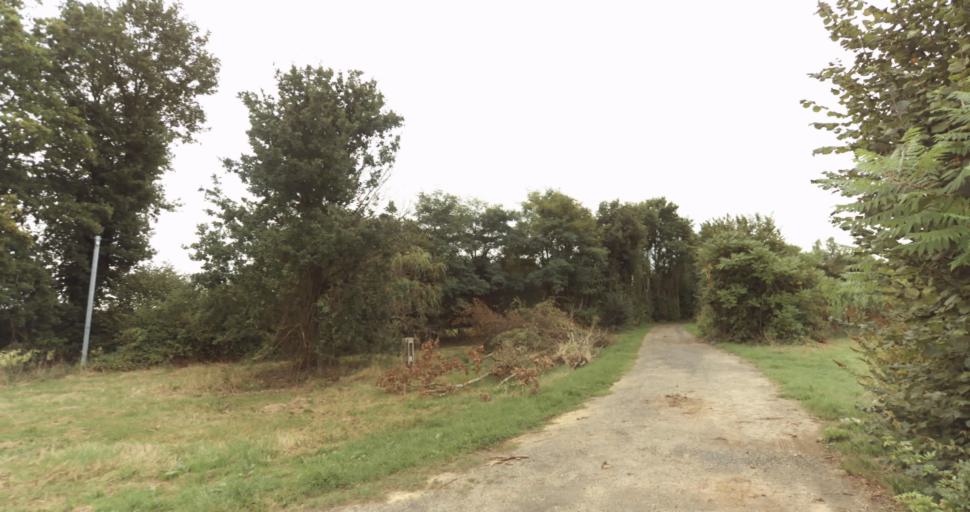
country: FR
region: Lower Normandy
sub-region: Departement de l'Orne
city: Gace
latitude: 48.7518
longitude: 0.3093
